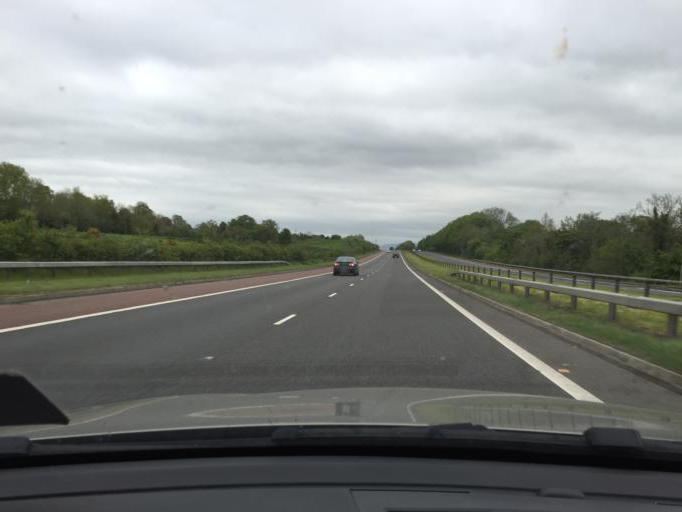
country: GB
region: Northern Ireland
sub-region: Banbridge District
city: Banbridge
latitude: 54.2680
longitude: -6.3120
